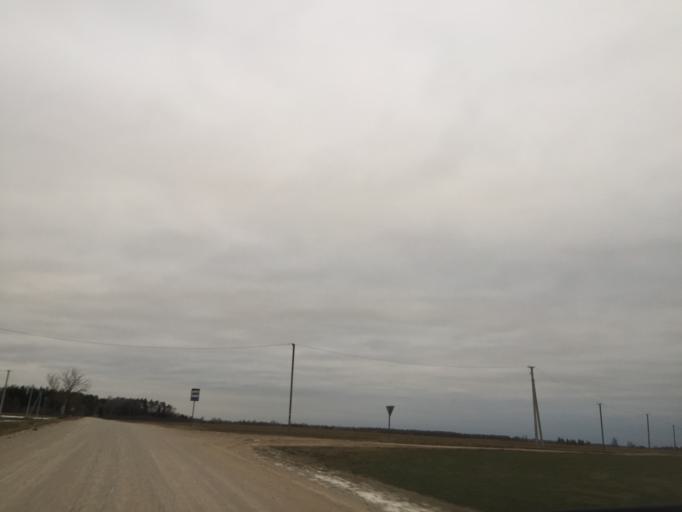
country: LT
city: Zagare
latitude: 56.2904
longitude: 23.2605
